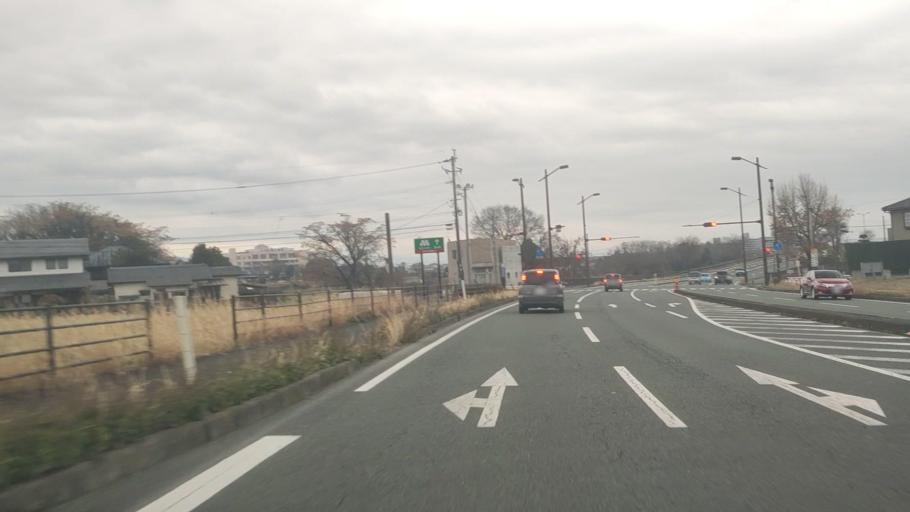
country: JP
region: Kumamoto
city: Ozu
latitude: 32.8222
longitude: 130.7912
